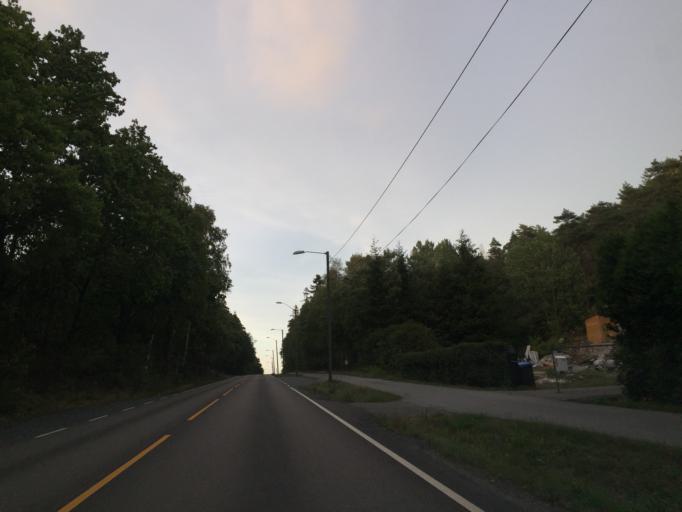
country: NO
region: Ostfold
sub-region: Fredrikstad
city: Fredrikstad
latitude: 59.1850
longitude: 10.9287
